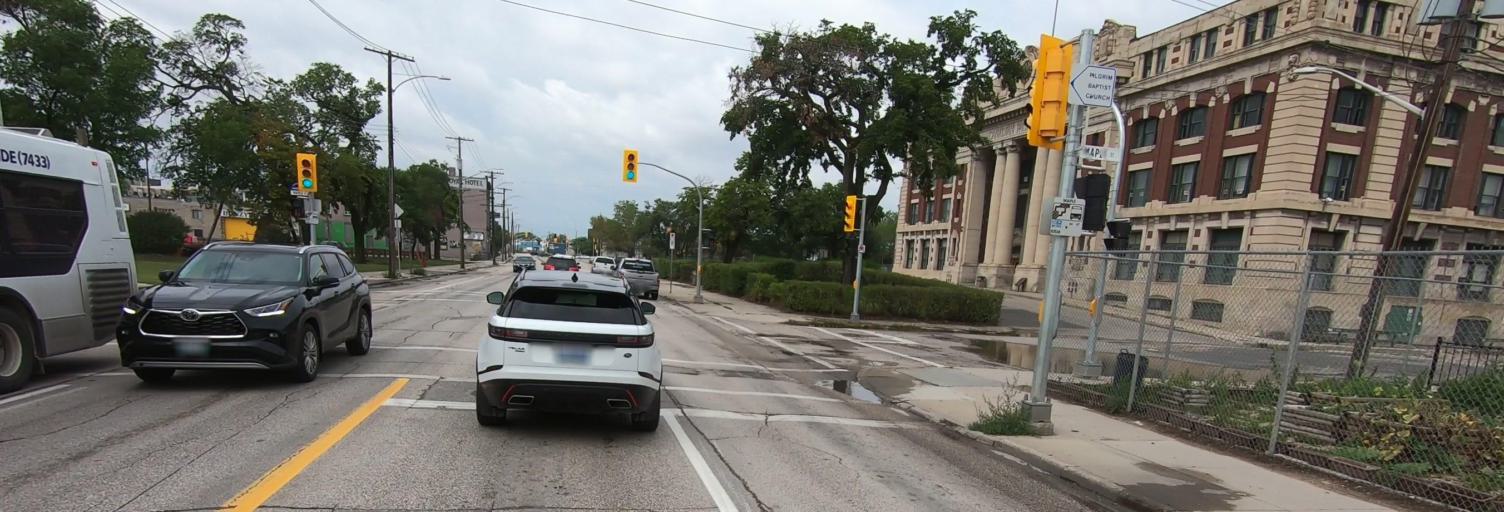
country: CA
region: Manitoba
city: Winnipeg
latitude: 49.9041
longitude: -97.1311
